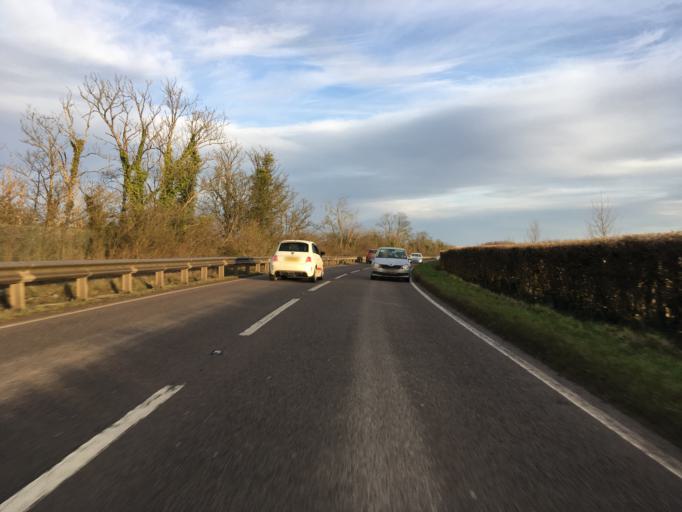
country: GB
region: England
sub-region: South Gloucestershire
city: Chipping Sodbury
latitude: 51.5447
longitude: -2.3977
